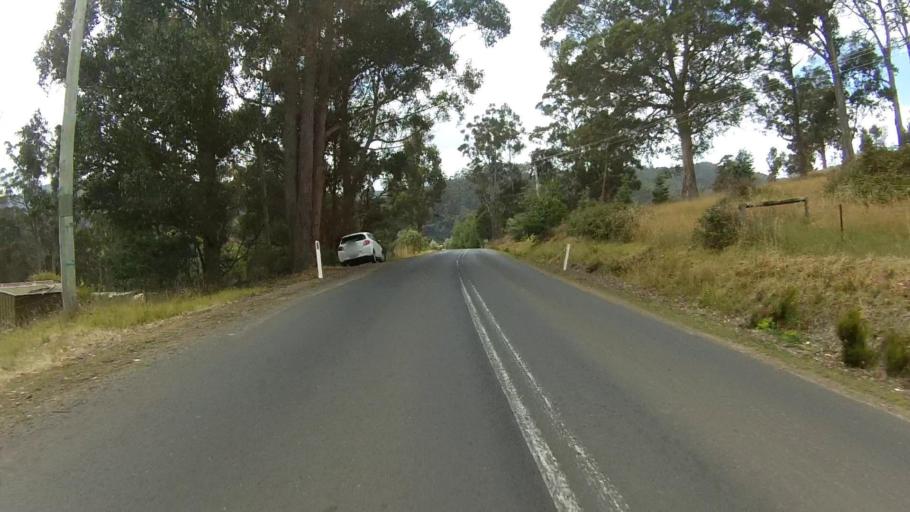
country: AU
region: Tasmania
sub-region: Huon Valley
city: Cygnet
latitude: -43.1372
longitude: 147.1525
